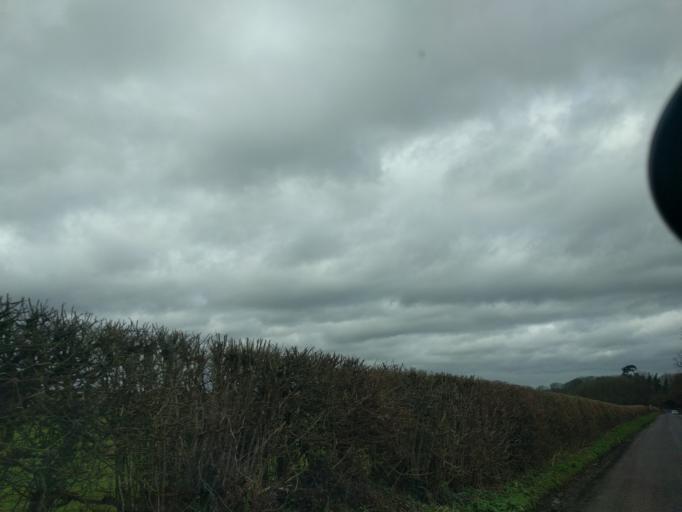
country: GB
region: England
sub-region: Wiltshire
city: Biddestone
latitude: 51.5008
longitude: -2.1952
